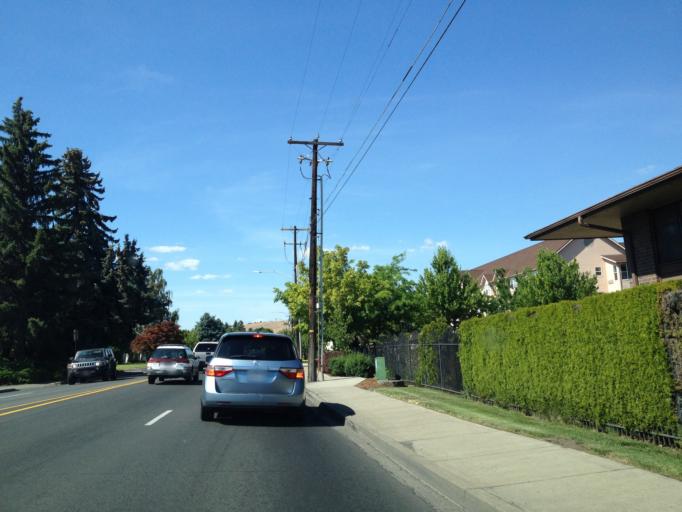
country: US
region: Washington
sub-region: Yakima County
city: West Valley
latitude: 46.6009
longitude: -120.5619
